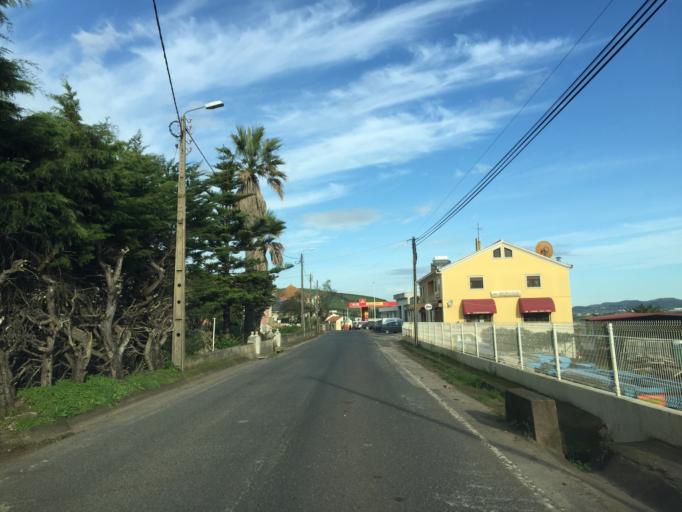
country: PT
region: Lisbon
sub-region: Sintra
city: Almargem
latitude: 38.8470
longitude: -9.2616
